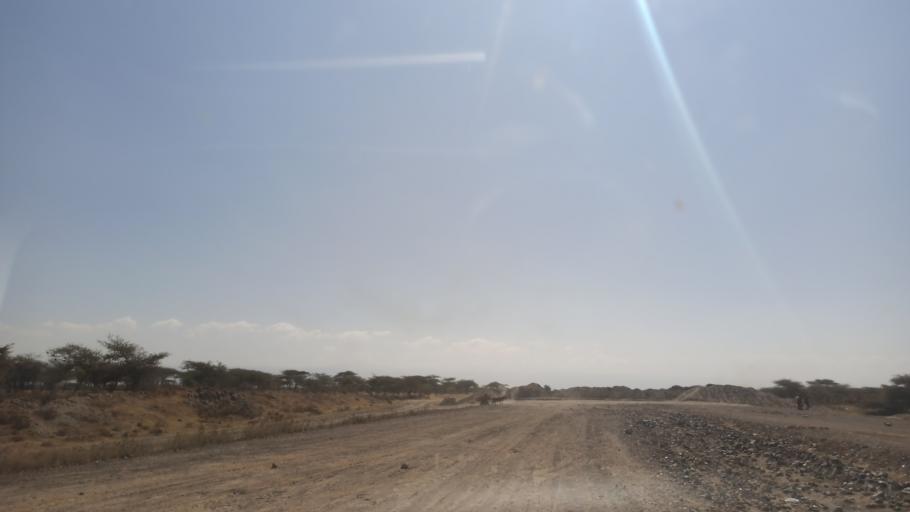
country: ET
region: Oromiya
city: Ziway
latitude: 7.6769
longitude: 38.6767
